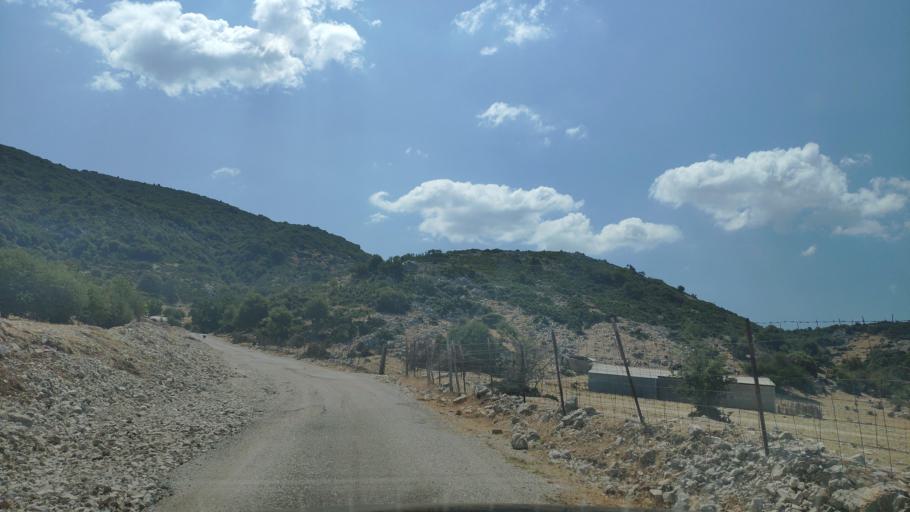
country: GR
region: West Greece
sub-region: Nomos Aitolias kai Akarnanias
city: Monastirakion
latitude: 38.8067
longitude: 20.9435
